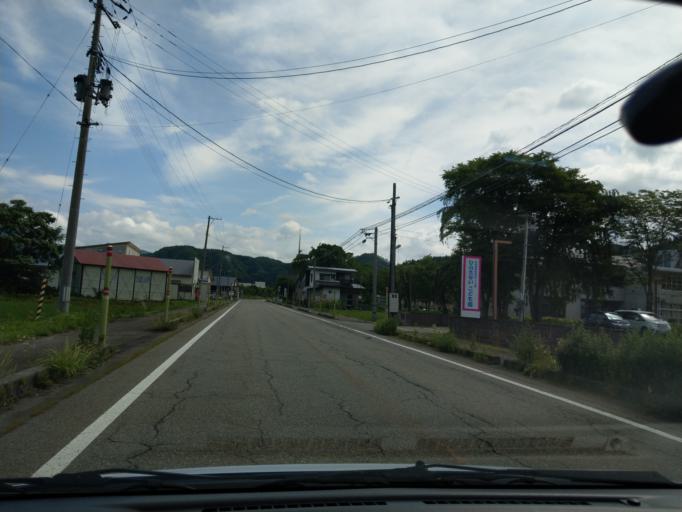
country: JP
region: Akita
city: Kakunodatemachi
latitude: 39.7407
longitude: 140.5880
